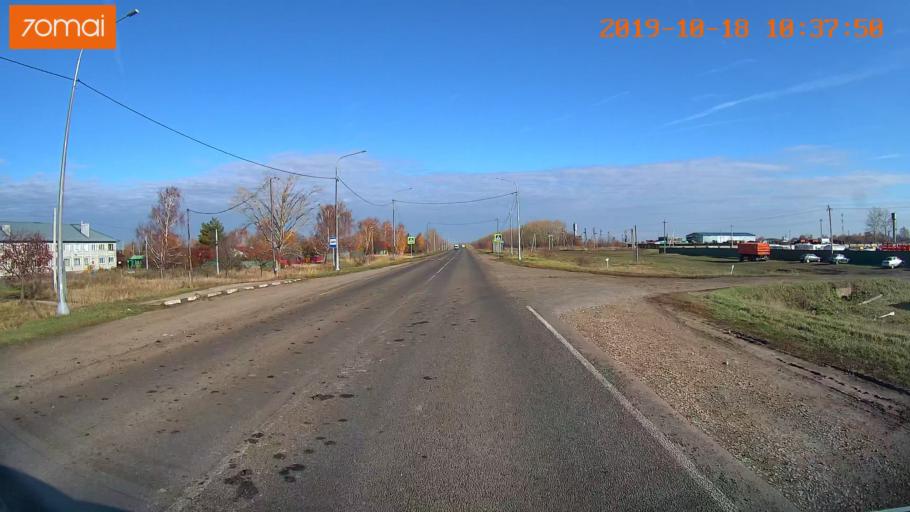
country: RU
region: Tula
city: Kurkino
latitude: 53.5655
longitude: 38.6352
